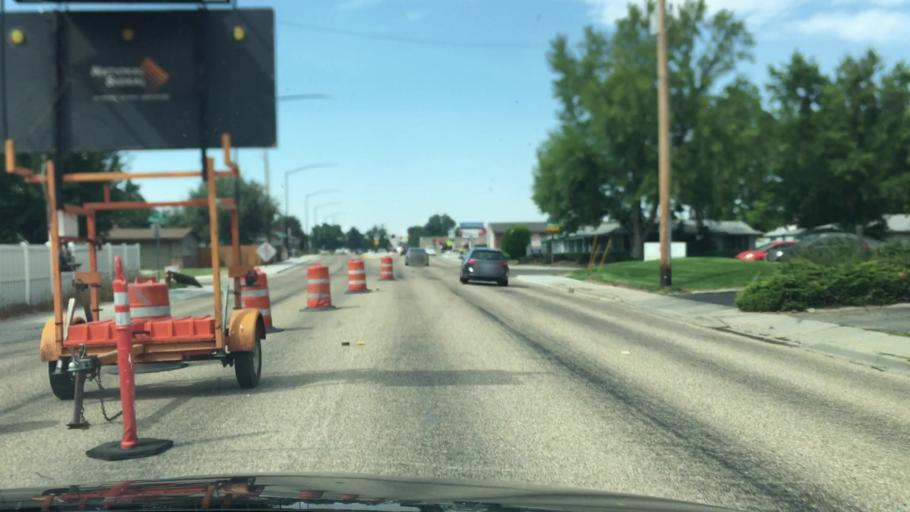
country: US
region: Idaho
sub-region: Ada County
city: Garden City
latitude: 43.6165
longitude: -116.2742
